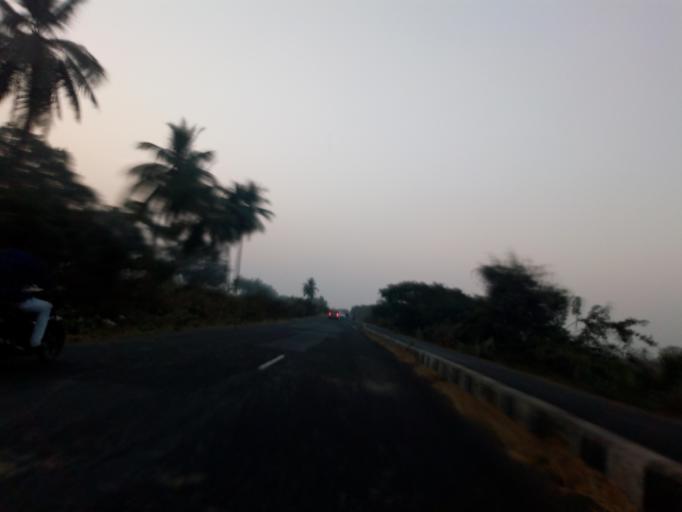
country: IN
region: Andhra Pradesh
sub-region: West Godavari
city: Tadepallegudem
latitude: 16.8236
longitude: 81.4646
